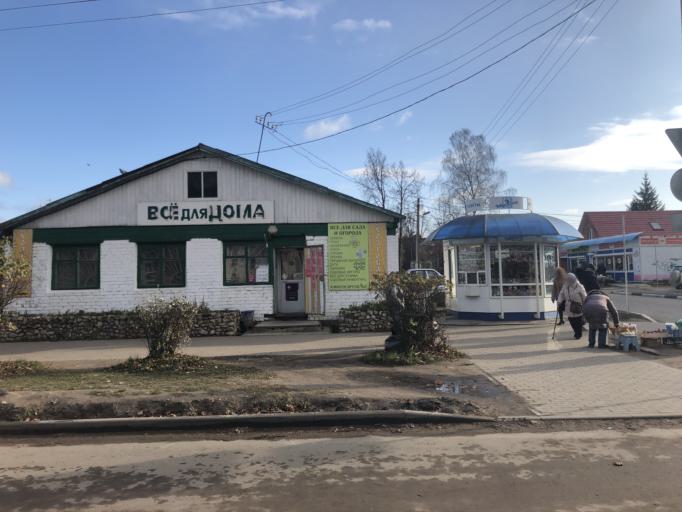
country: RU
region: Tverskaya
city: Rzhev
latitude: 56.2498
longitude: 34.3274
